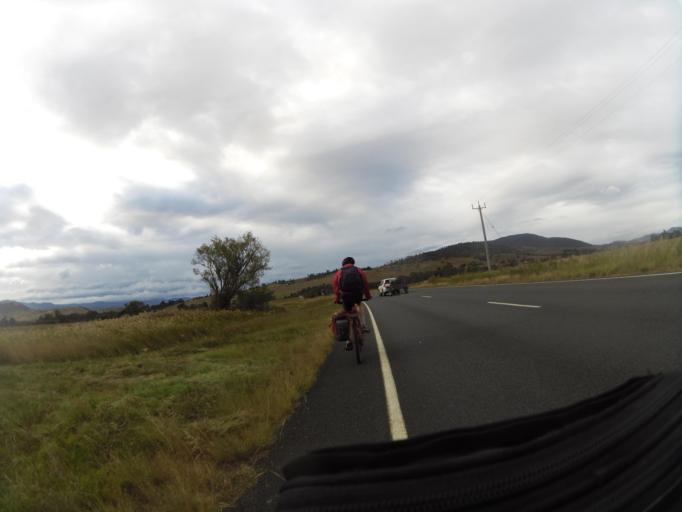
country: AU
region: New South Wales
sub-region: Snowy River
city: Jindabyne
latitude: -36.1193
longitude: 147.9812
